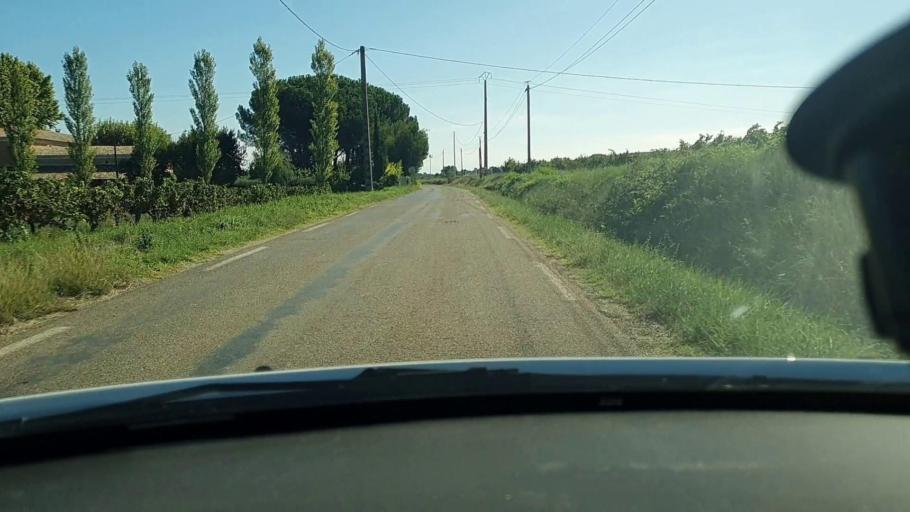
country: FR
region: Languedoc-Roussillon
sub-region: Departement du Gard
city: Saint-Paulet-de-Caisson
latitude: 44.2638
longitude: 4.5850
